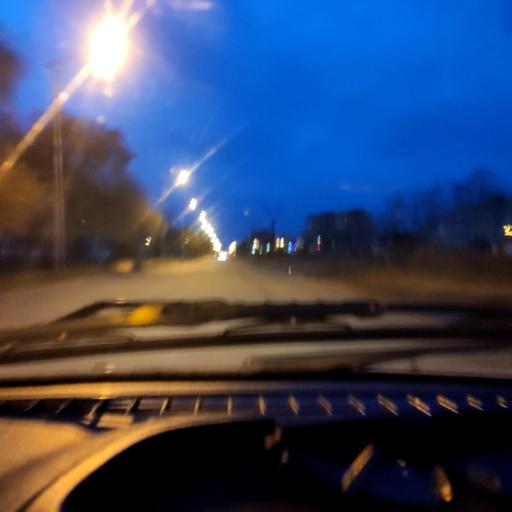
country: RU
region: Samara
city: Zhigulevsk
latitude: 53.4786
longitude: 49.4931
